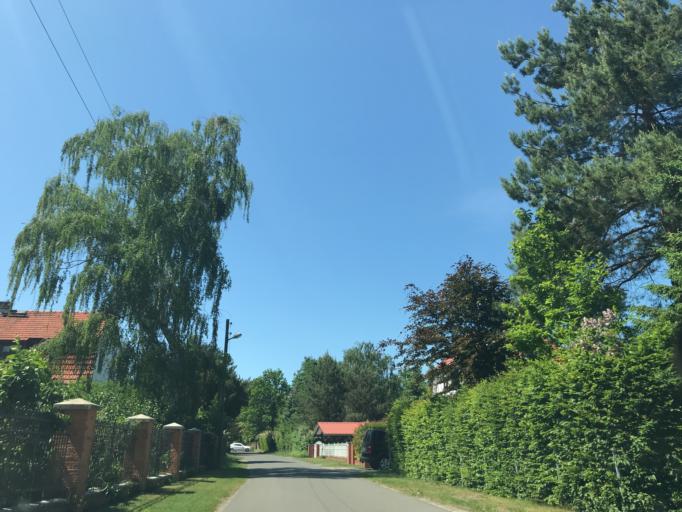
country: DE
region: Berlin
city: Falkenhagener Feld
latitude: 52.5672
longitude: 13.1475
